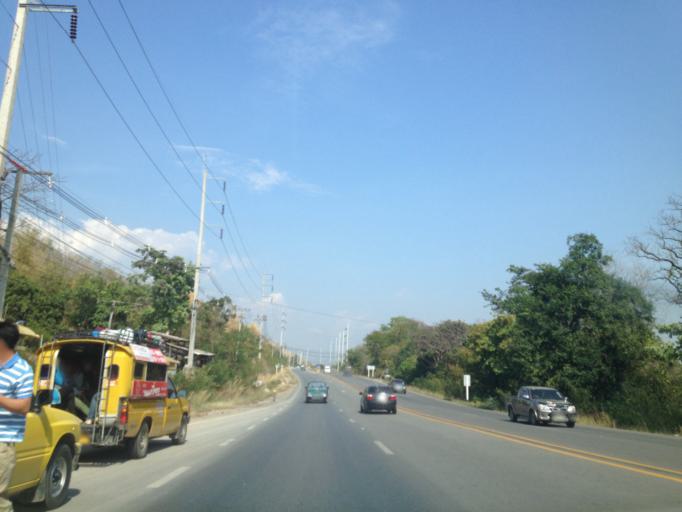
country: TH
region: Chiang Mai
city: Chom Thong
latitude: 18.3663
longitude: 98.6800
